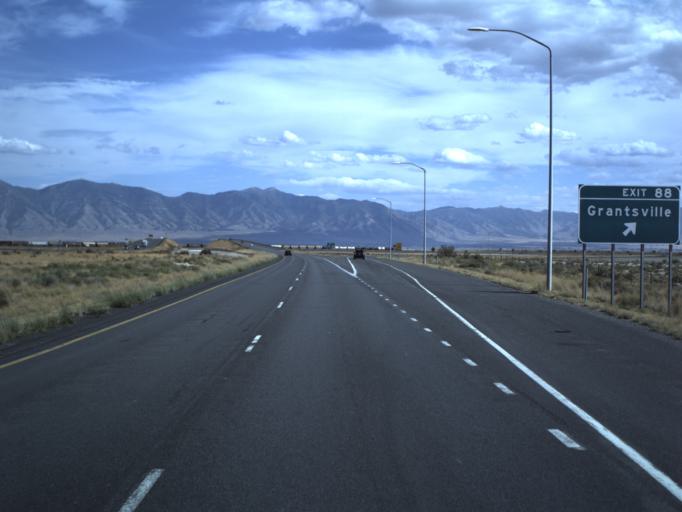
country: US
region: Utah
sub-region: Tooele County
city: Grantsville
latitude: 40.6864
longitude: -112.4516
